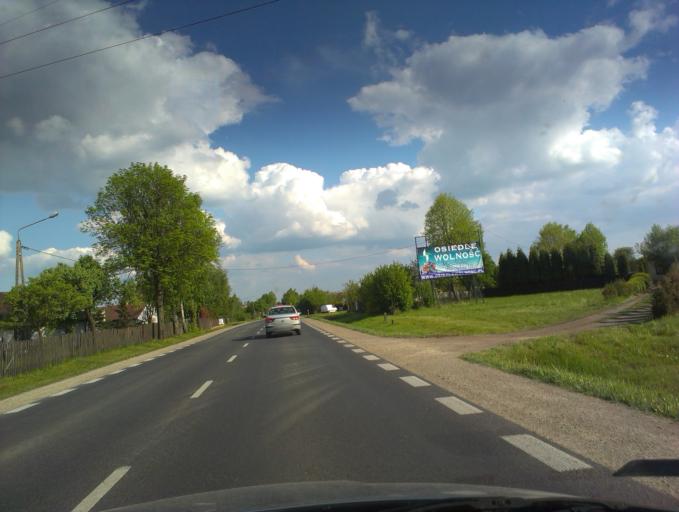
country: PL
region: Masovian Voivodeship
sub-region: Powiat radomski
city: Skaryszew
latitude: 51.3454
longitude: 21.2230
